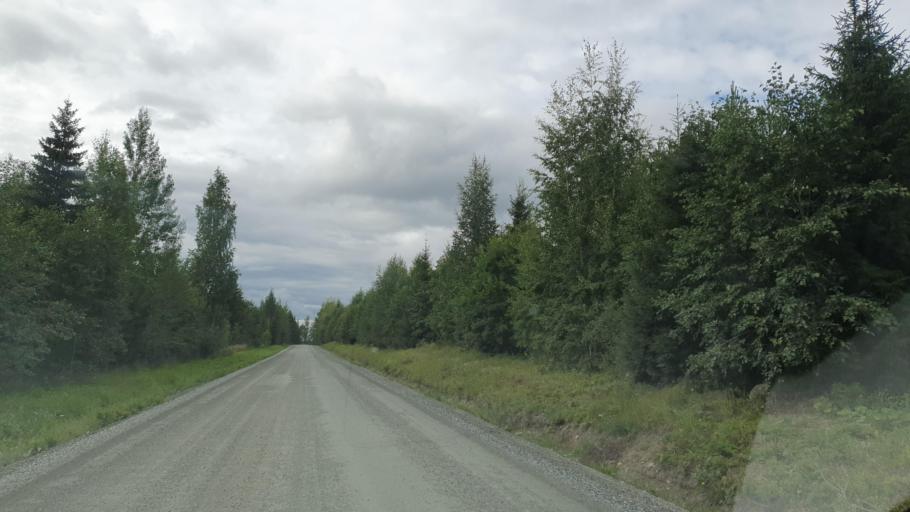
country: FI
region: Northern Savo
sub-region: Ylae-Savo
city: Iisalmi
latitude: 63.5163
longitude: 27.1090
